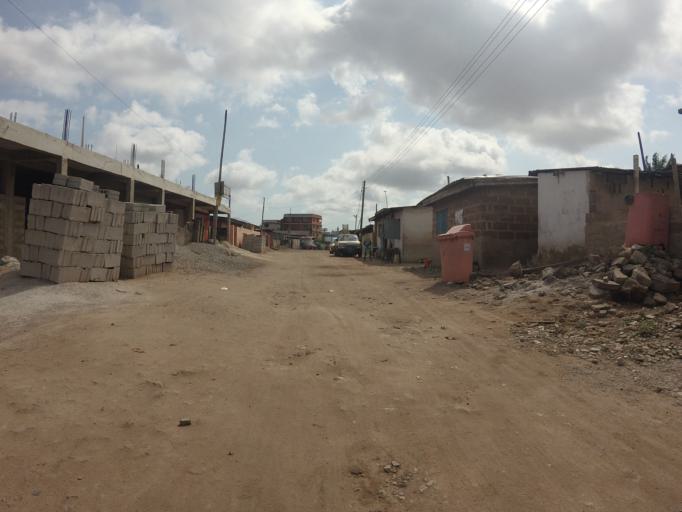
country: GH
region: Greater Accra
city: Dome
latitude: 5.6154
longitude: -0.2448
